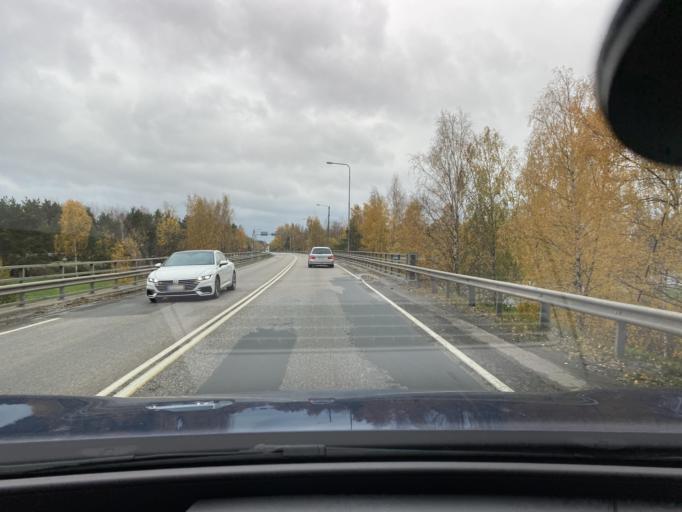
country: FI
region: Satakunta
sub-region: Rauma
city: Rauma
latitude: 61.1329
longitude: 21.5351
